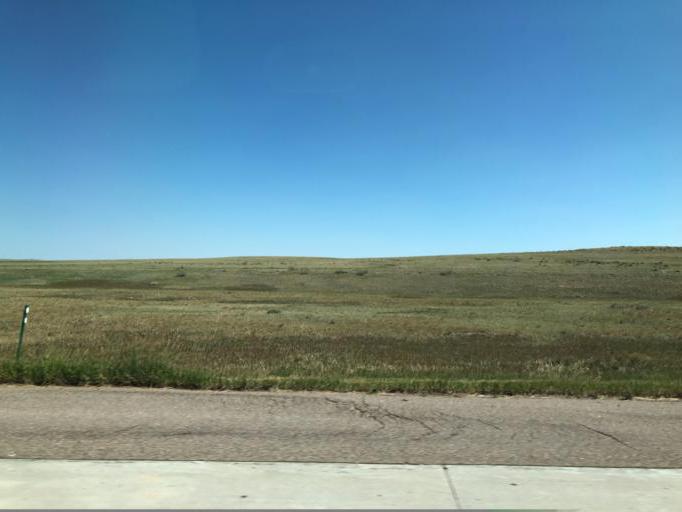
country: US
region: Colorado
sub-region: Lincoln County
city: Limon
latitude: 39.2734
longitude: -103.7309
